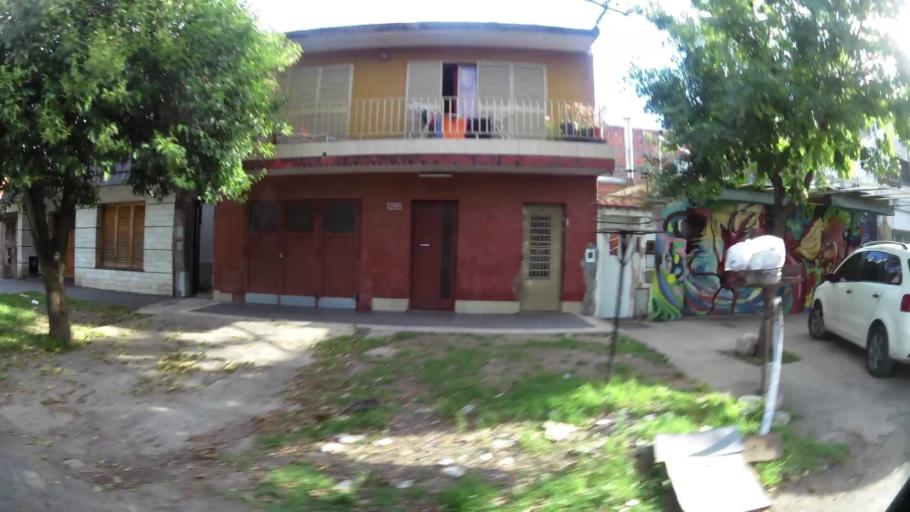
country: AR
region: Santa Fe
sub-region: Departamento de Rosario
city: Rosario
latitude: -32.9782
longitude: -60.6713
